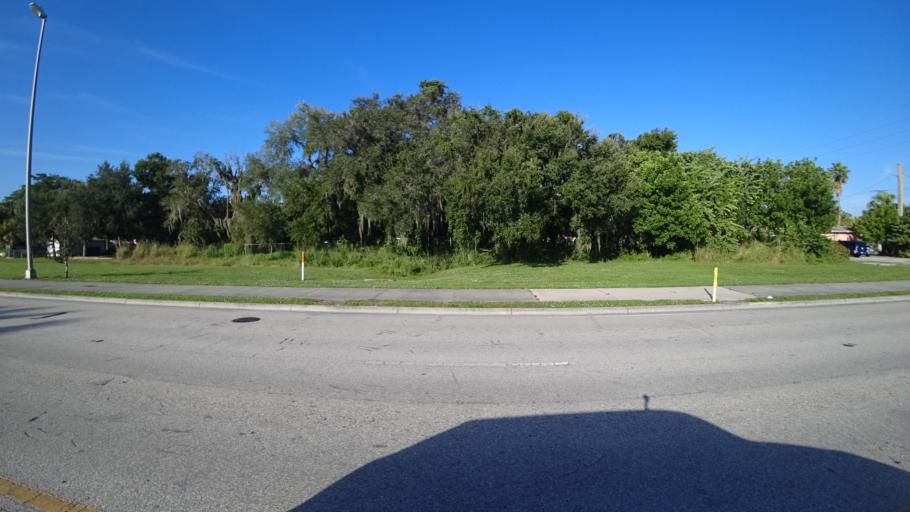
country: US
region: Florida
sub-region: Manatee County
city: Bradenton
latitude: 27.4910
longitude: -82.5548
